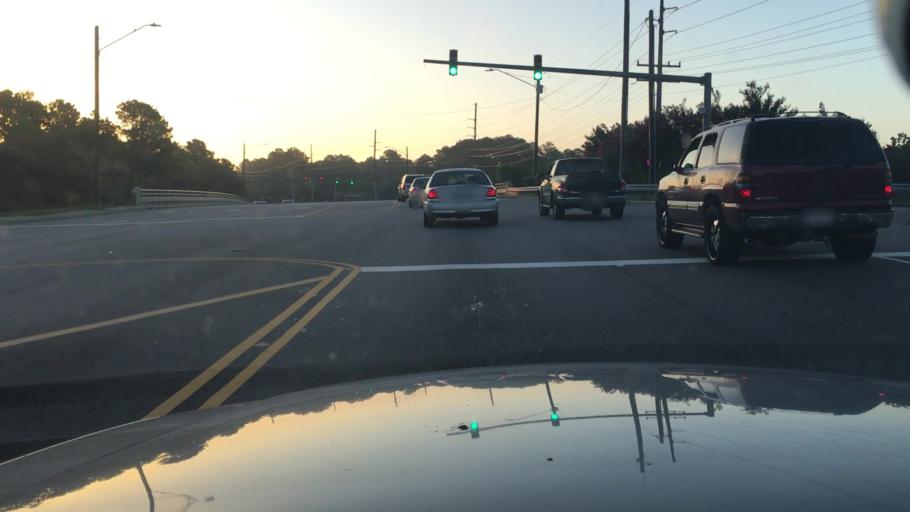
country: US
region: North Carolina
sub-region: Cumberland County
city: Fayetteville
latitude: 35.0593
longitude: -78.9549
